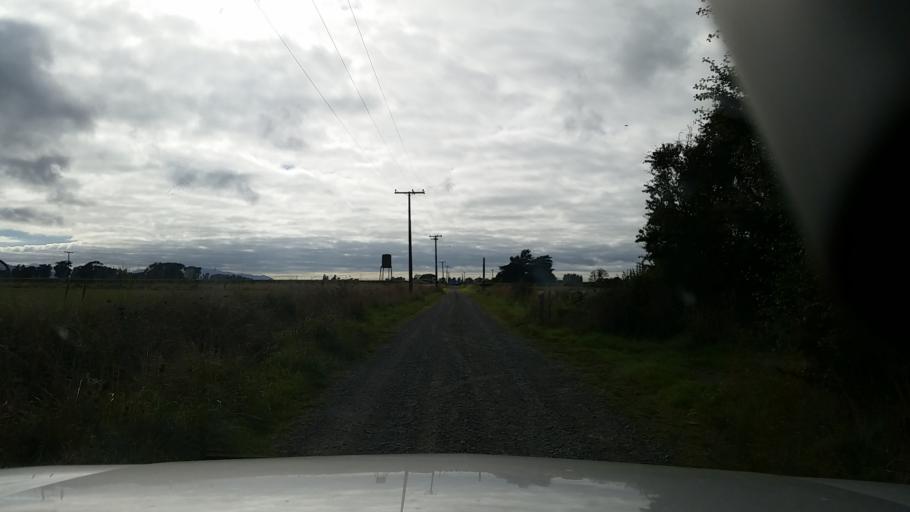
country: NZ
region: Marlborough
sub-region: Marlborough District
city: Blenheim
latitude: -41.4644
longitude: 173.9899
